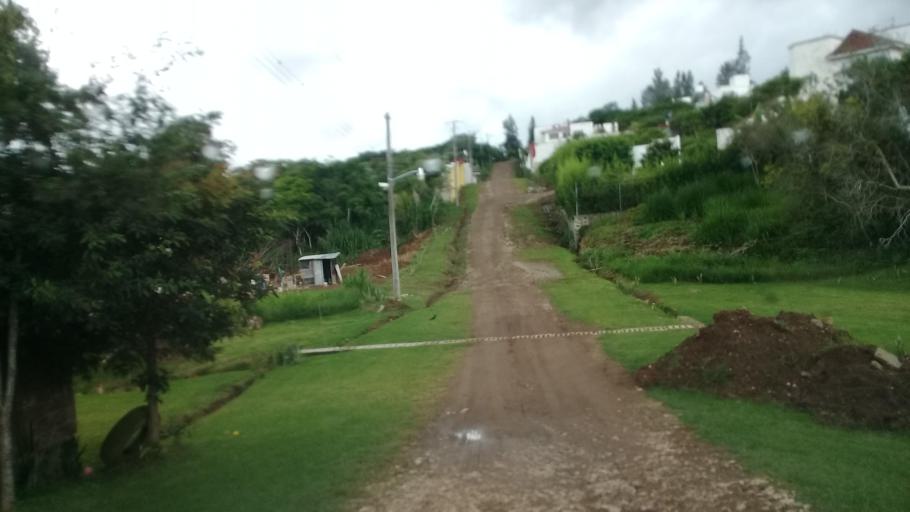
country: MX
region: Veracruz
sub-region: Emiliano Zapata
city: Jacarandas
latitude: 19.5083
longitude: -96.8492
